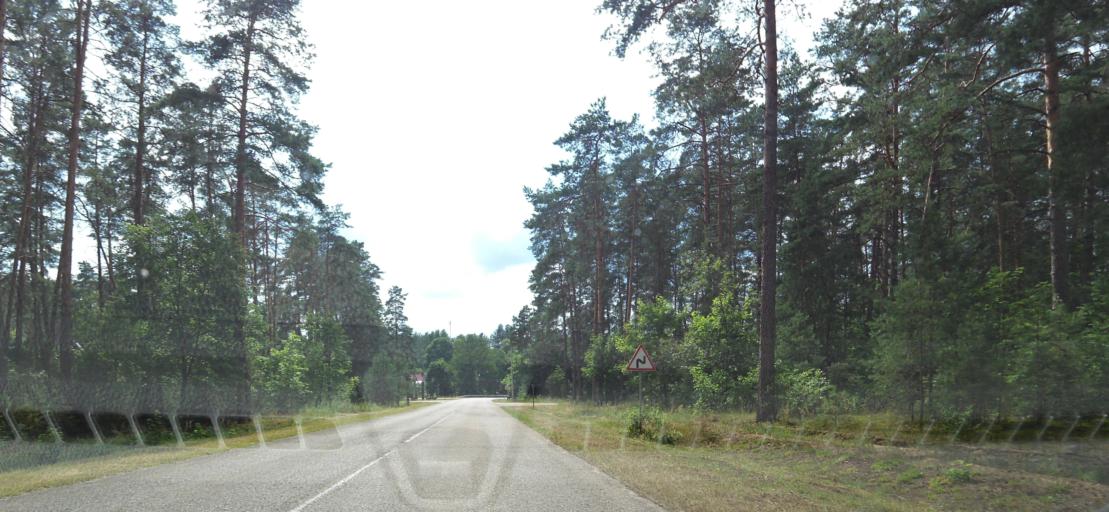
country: LT
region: Alytaus apskritis
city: Druskininkai
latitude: 53.9889
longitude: 24.1008
